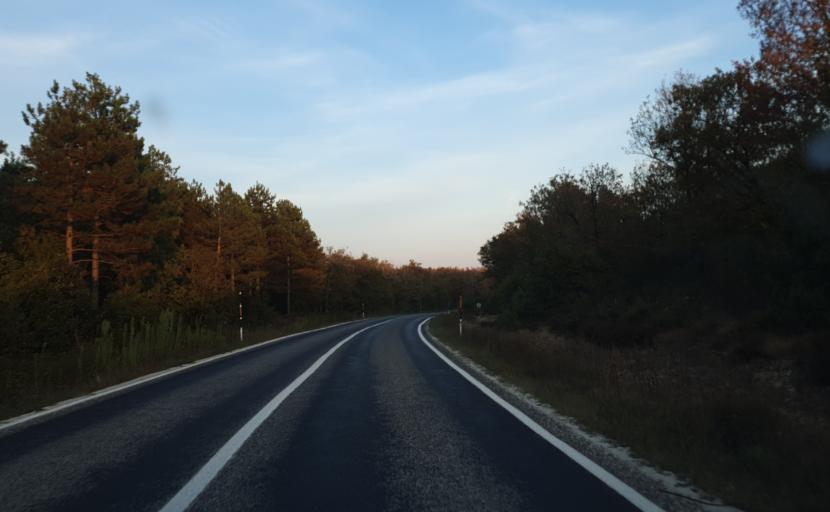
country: TR
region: Kirklareli
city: Igneada
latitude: 41.8671
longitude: 27.8522
